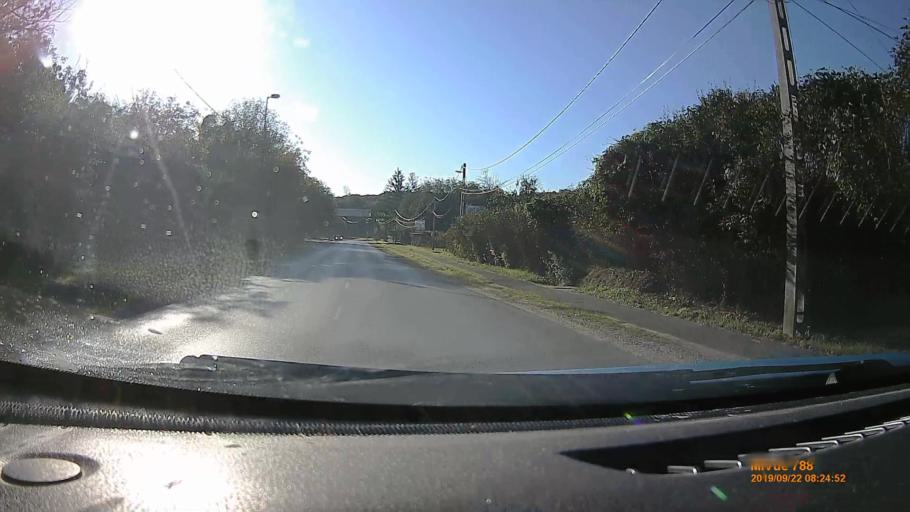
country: HU
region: Borsod-Abauj-Zemplen
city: Miskolc
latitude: 48.0886
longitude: 20.7136
